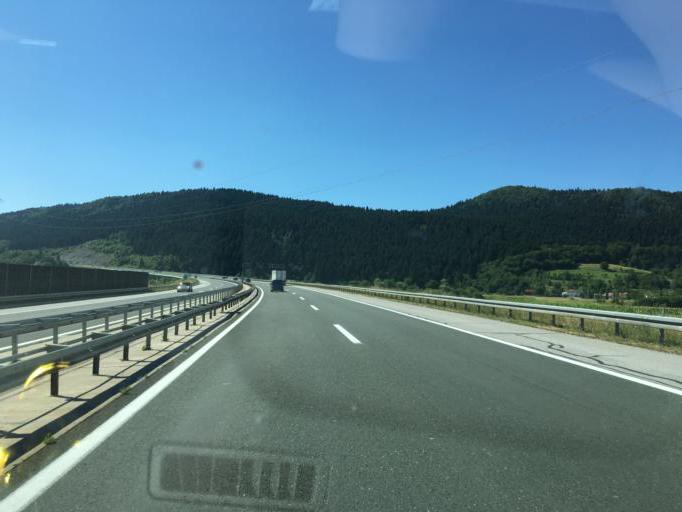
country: HR
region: Licko-Senjska
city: Otocac
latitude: 44.8675
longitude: 15.2077
